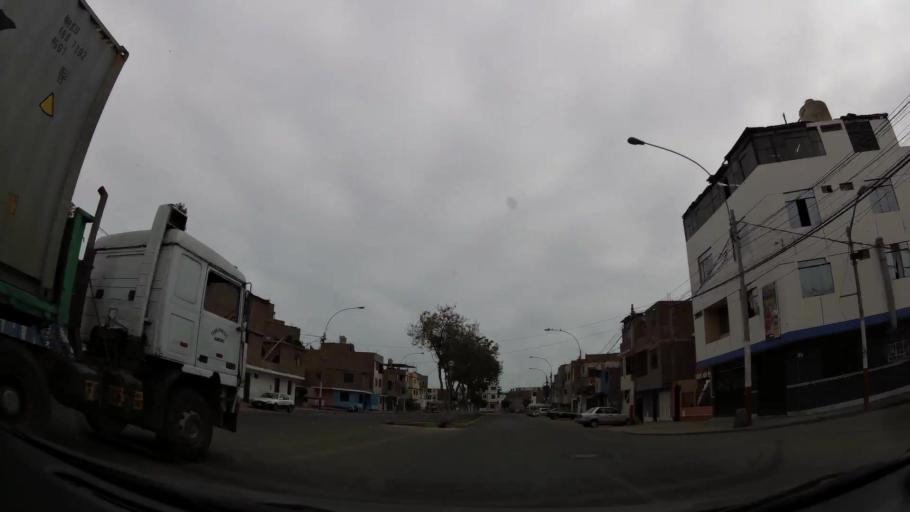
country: PE
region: Callao
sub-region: Callao
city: Callao
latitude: -12.0549
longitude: -77.1212
